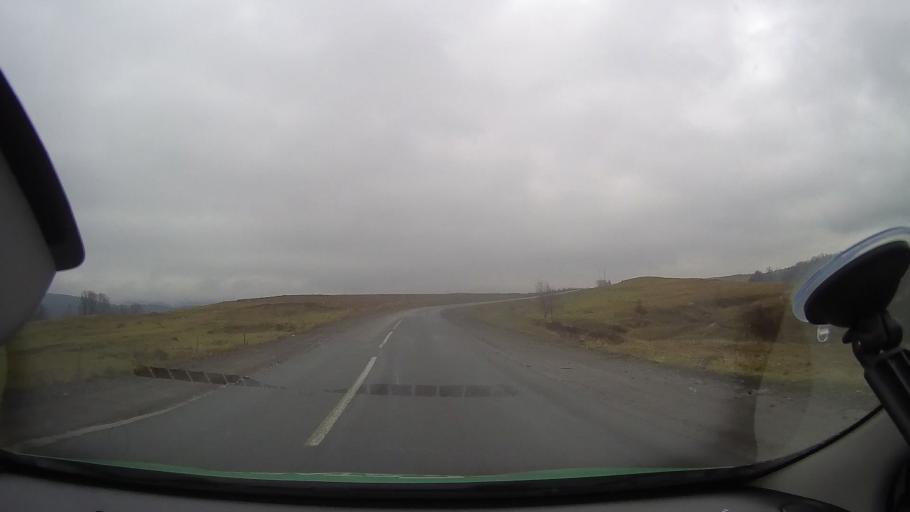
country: RO
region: Arad
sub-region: Comuna Halmagiu
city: Halmagiu
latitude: 46.2876
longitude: 22.5594
